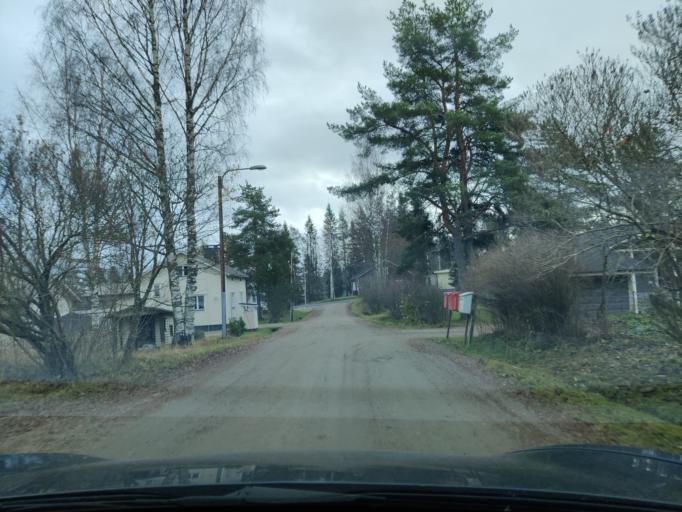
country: FI
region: Northern Savo
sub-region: Ylae-Savo
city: Kiuruvesi
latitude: 63.6488
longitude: 26.6317
